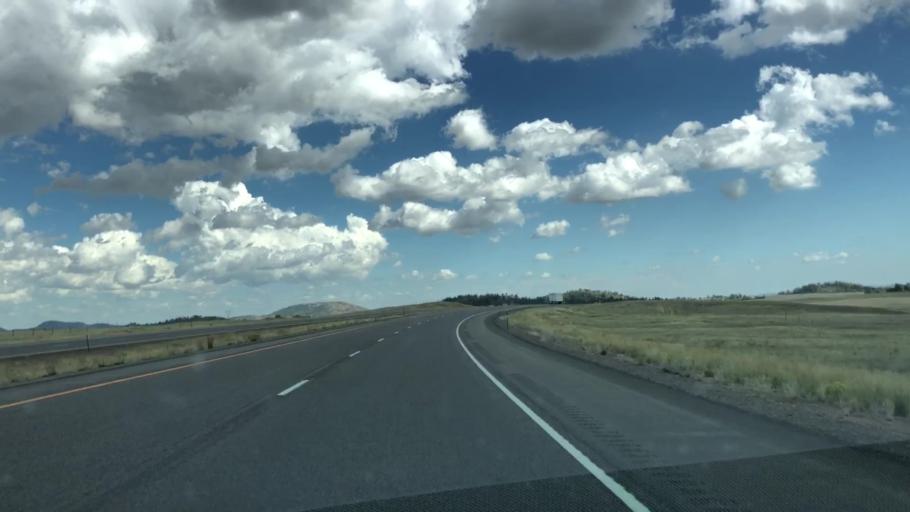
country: US
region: Wyoming
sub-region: Albany County
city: Laramie
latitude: 41.0265
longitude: -105.4290
